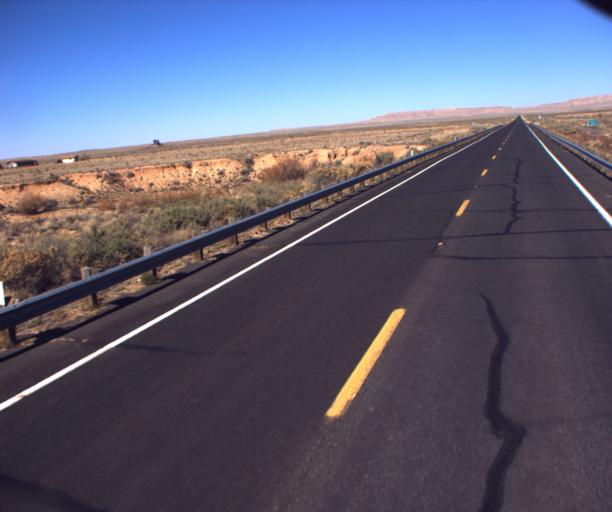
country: US
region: Arizona
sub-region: Navajo County
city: First Mesa
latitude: 35.7072
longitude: -110.5100
